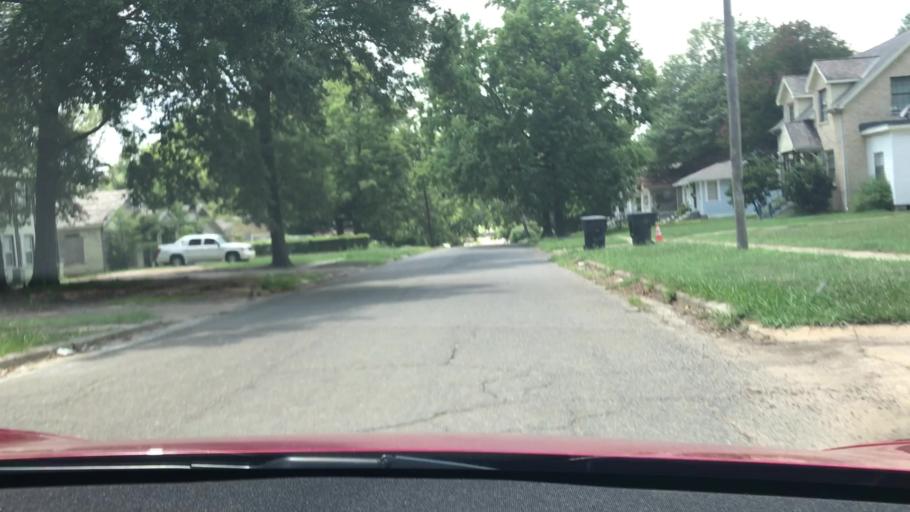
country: US
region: Louisiana
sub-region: Bossier Parish
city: Bossier City
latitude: 32.4963
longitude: -93.7291
